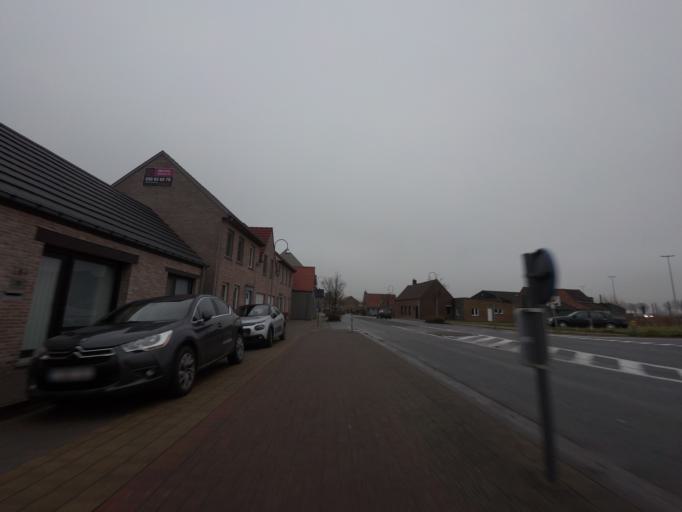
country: BE
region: Flanders
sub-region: Provincie West-Vlaanderen
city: Knokke-Heist
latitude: 51.3108
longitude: 3.3002
